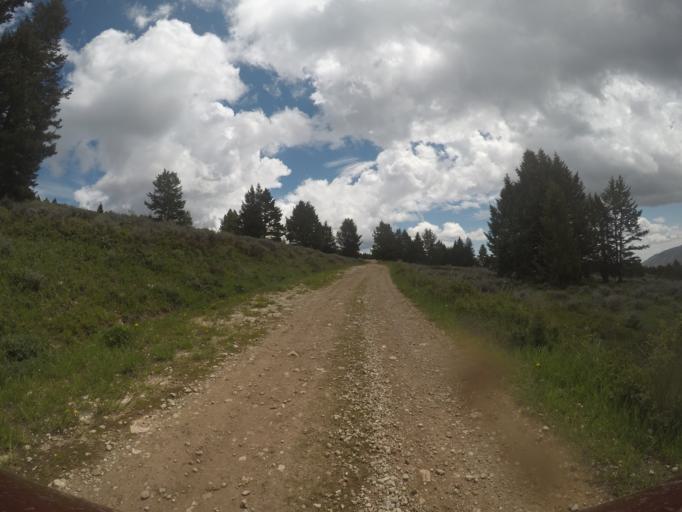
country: US
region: Wyoming
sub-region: Big Horn County
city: Lovell
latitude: 45.1692
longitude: -108.4257
